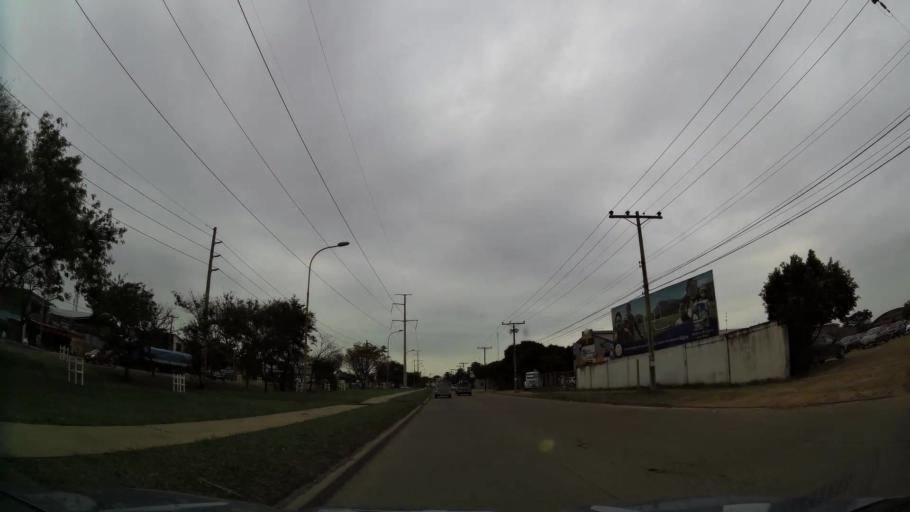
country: BO
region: Santa Cruz
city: Santa Cruz de la Sierra
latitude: -17.7739
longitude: -63.1469
